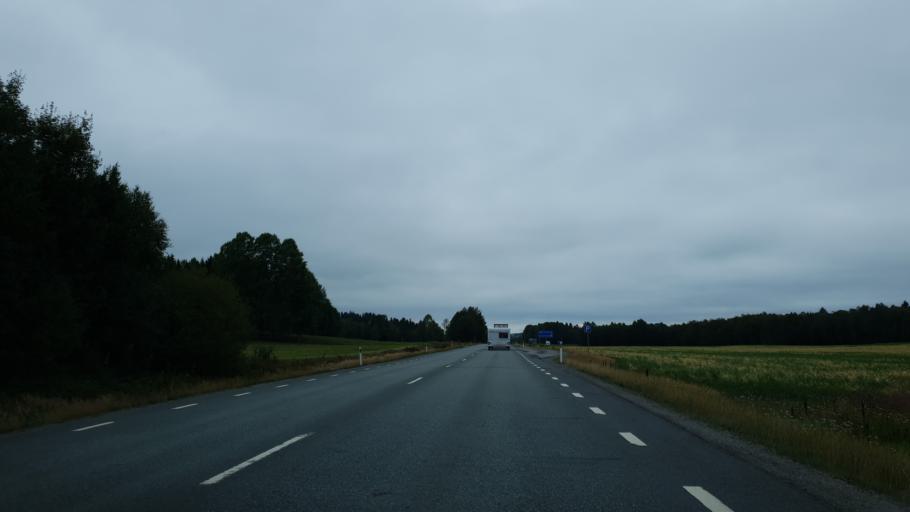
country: SE
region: Vaesterbotten
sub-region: Skelleftea Kommun
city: Burea
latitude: 64.3864
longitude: 21.3005
